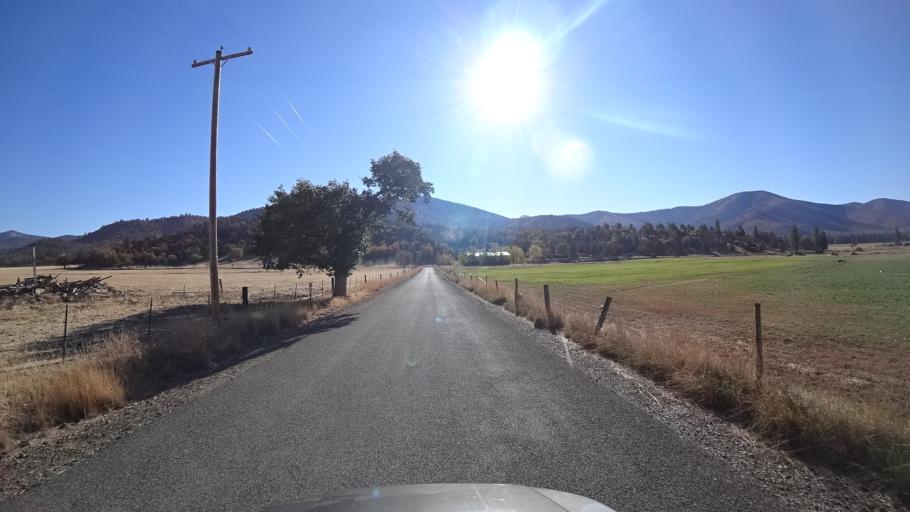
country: US
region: California
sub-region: Siskiyou County
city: Yreka
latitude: 41.5800
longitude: -122.7911
